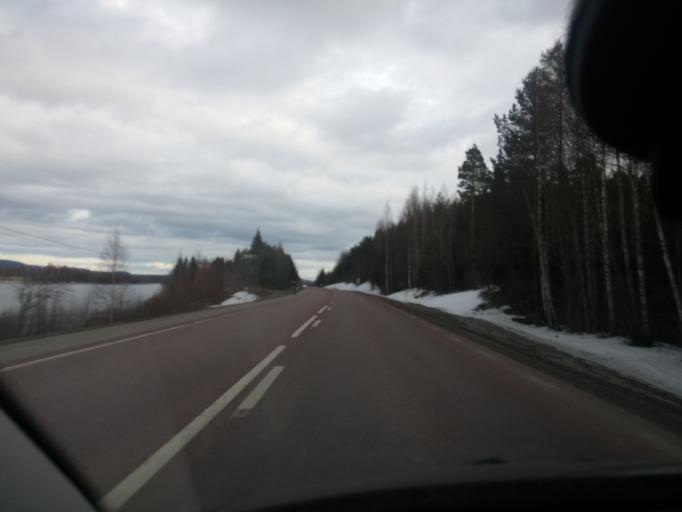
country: SE
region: Gaevleborg
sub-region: Ljusdals Kommun
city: Ljusdal
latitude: 61.8177
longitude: 16.0705
